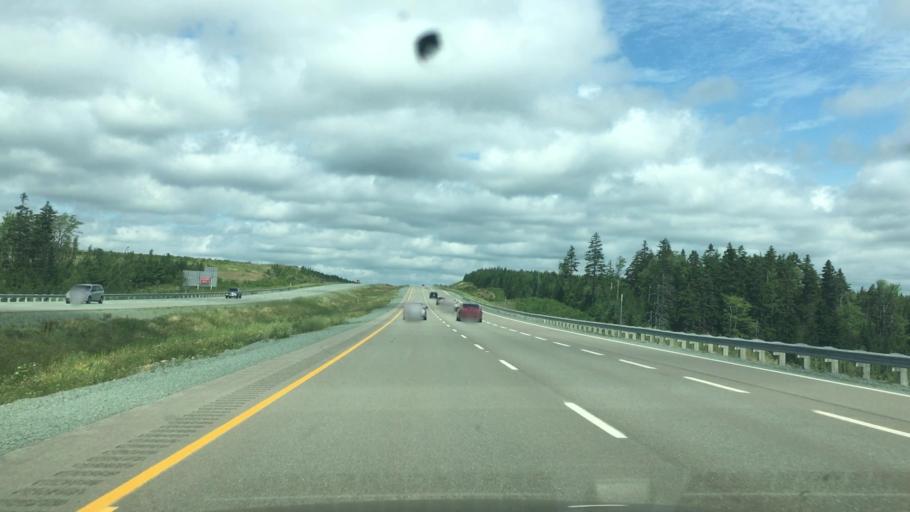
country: CA
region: Nova Scotia
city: Oxford
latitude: 45.6122
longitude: -63.7378
